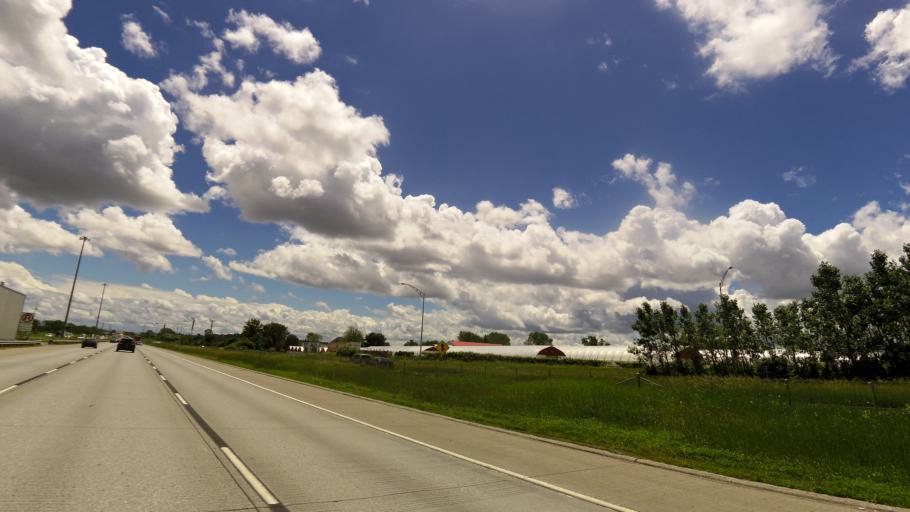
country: CA
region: Quebec
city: Dollard-Des Ormeaux
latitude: 45.5240
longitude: -73.7774
